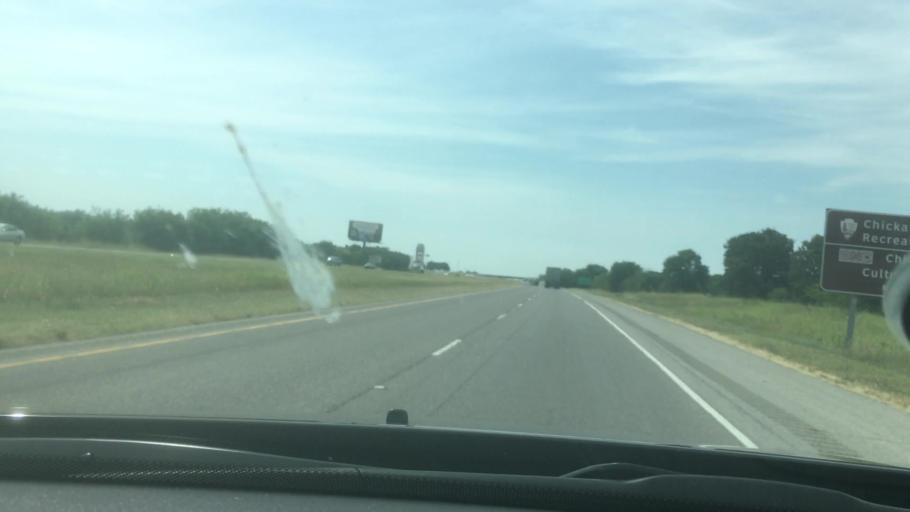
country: US
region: Oklahoma
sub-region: Murray County
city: Davis
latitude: 34.5167
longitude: -97.1817
